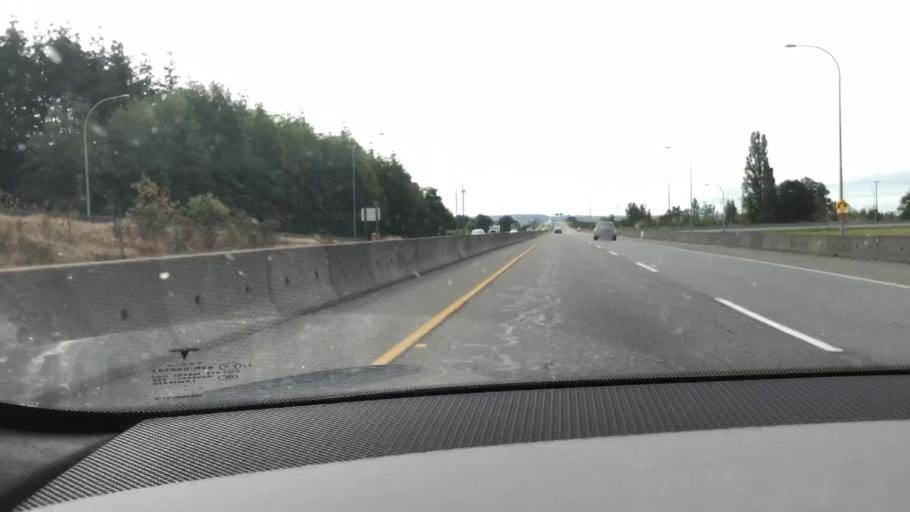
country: CA
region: British Columbia
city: Delta
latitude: 49.1021
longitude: -122.9003
